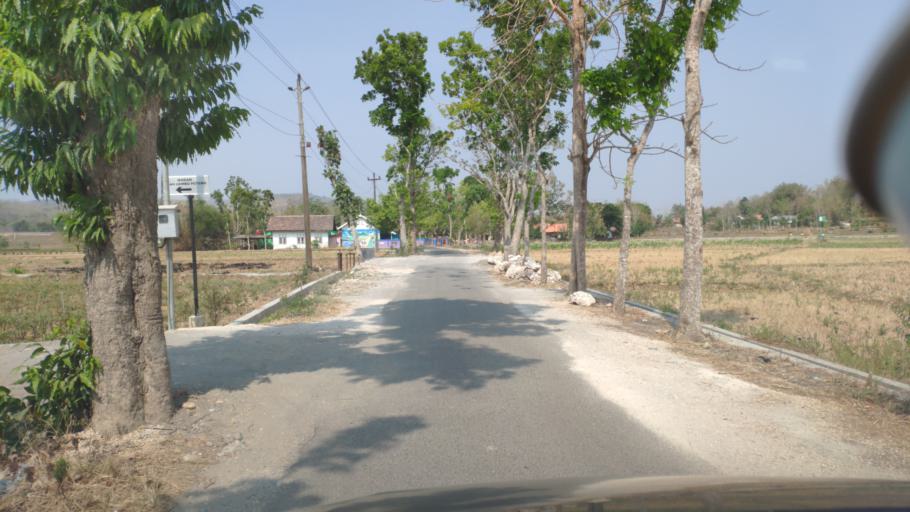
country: ID
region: Central Java
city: Tempuran
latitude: -6.9116
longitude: 111.4572
